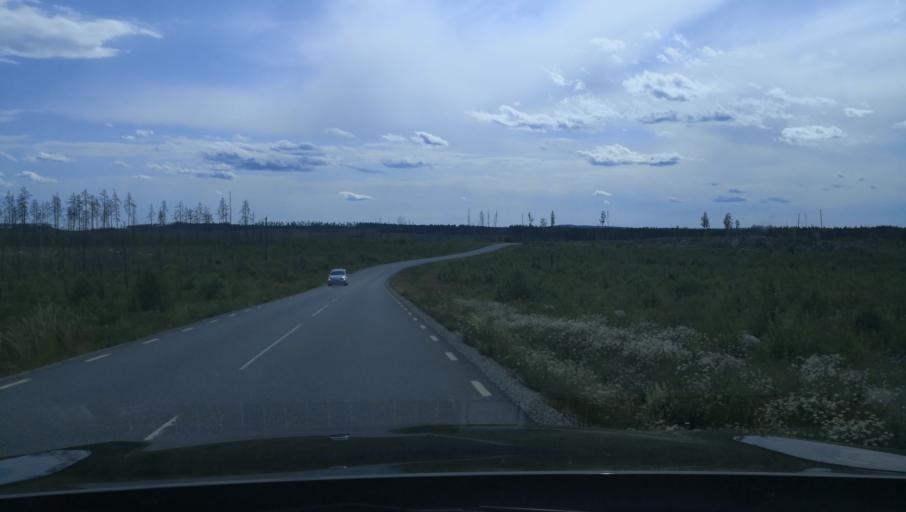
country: SE
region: Vaestmanland
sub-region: Norbergs Kommun
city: Norberg
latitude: 59.9796
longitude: 16.0441
